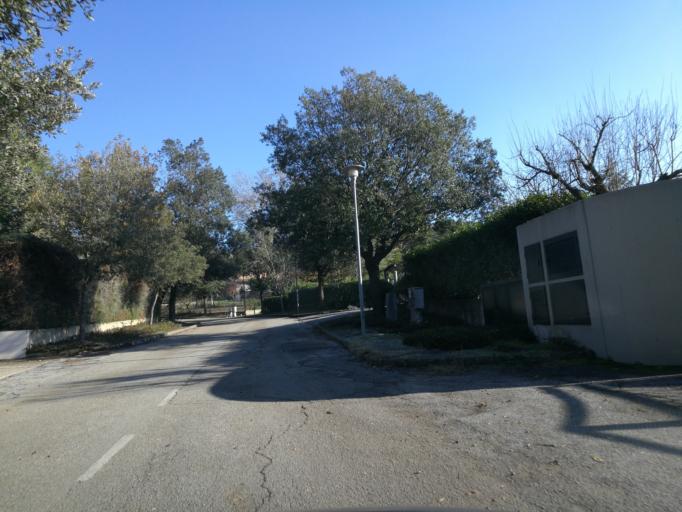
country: IT
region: Umbria
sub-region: Provincia di Perugia
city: Perugia
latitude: 43.0813
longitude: 12.3717
